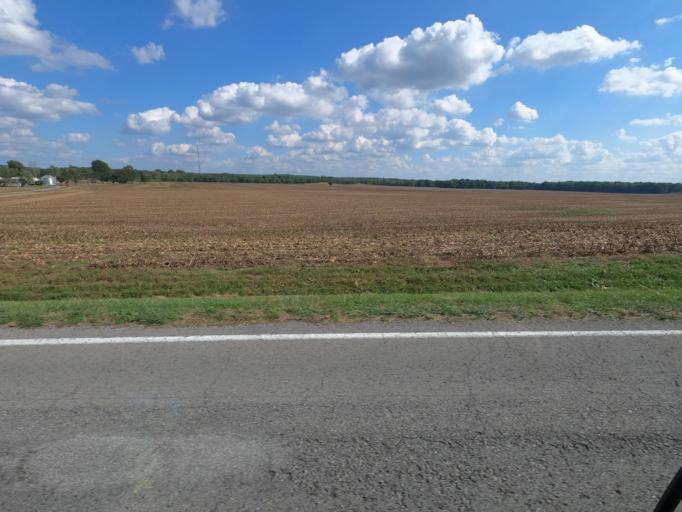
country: US
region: Illinois
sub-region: Massac County
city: Metropolis
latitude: 37.2751
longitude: -88.7551
